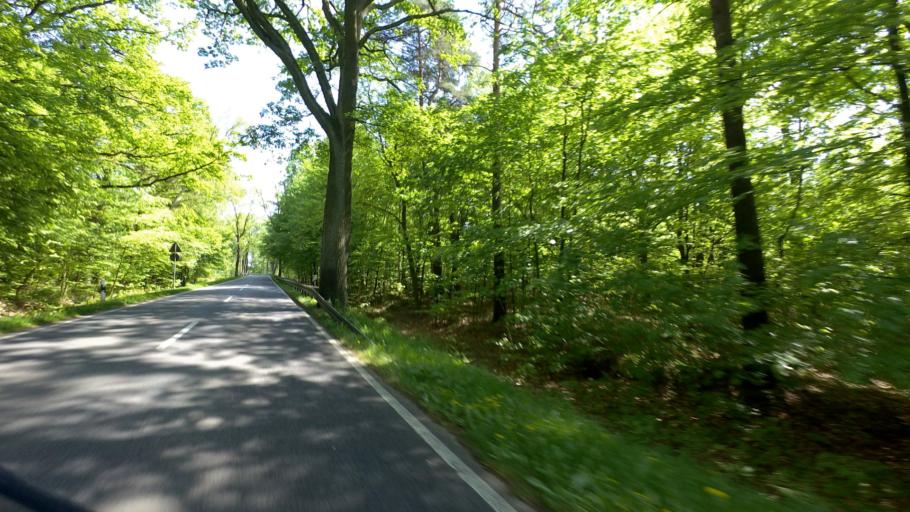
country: DE
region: Brandenburg
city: Schlepzig
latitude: 52.0628
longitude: 13.9213
